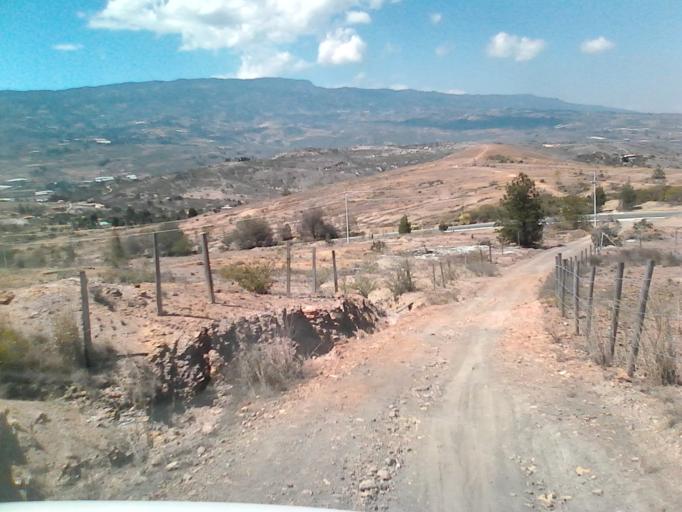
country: CO
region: Boyaca
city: Villa de Leiva
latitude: 5.6228
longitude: -73.5723
